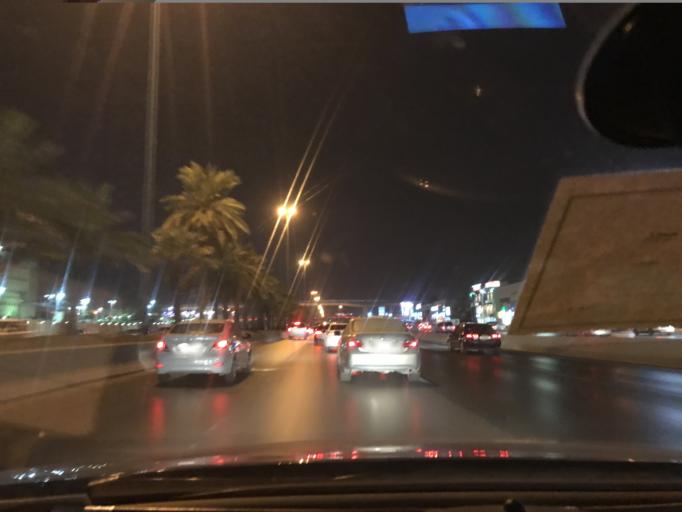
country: SA
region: Ar Riyad
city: Riyadh
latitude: 24.7562
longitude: 46.7408
